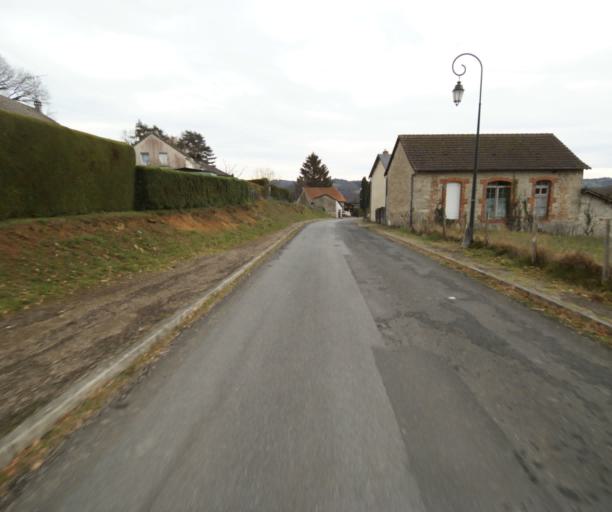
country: FR
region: Limousin
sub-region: Departement de la Correze
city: Chameyrat
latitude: 45.2362
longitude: 1.6969
